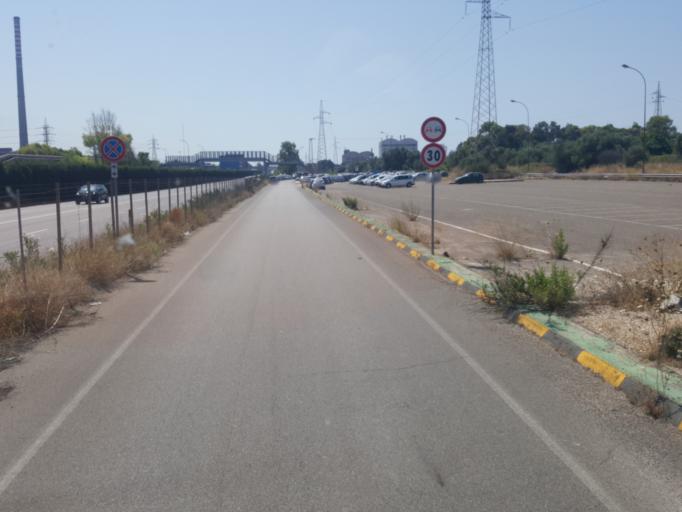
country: IT
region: Apulia
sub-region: Provincia di Taranto
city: Statte
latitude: 40.5057
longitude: 17.1962
